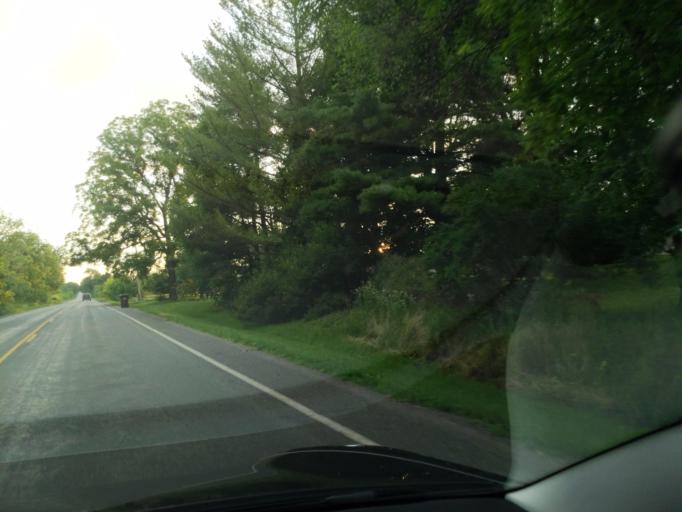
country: US
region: Michigan
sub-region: Ingham County
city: Mason
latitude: 42.5240
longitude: -84.4188
